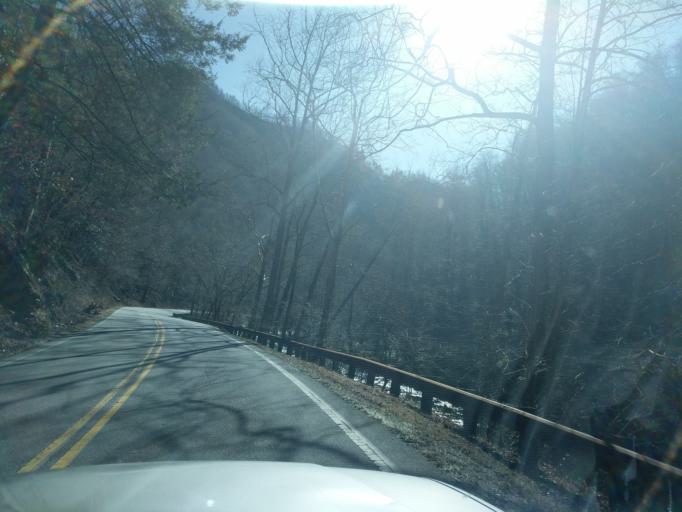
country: US
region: North Carolina
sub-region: Graham County
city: Robbinsville
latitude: 35.3270
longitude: -83.6310
